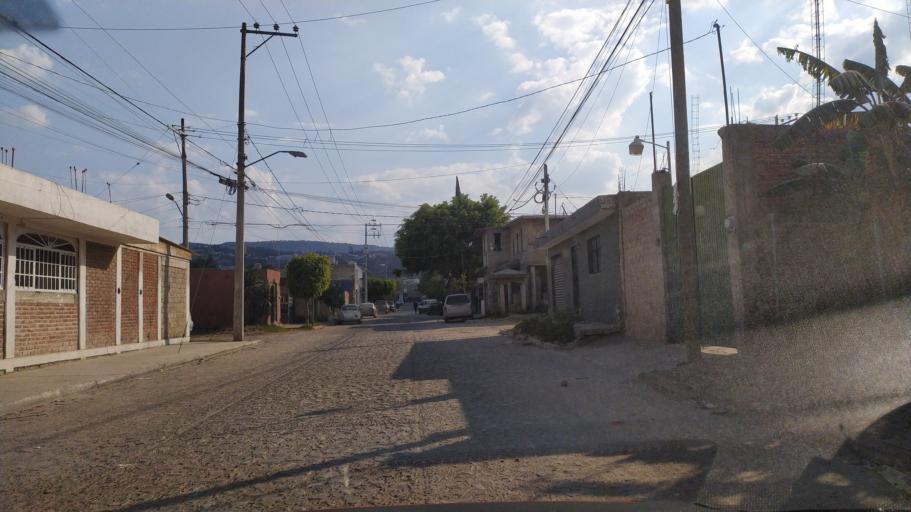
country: MX
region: Jalisco
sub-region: Tlajomulco de Zuniga
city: Palomar
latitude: 20.6303
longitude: -103.4723
